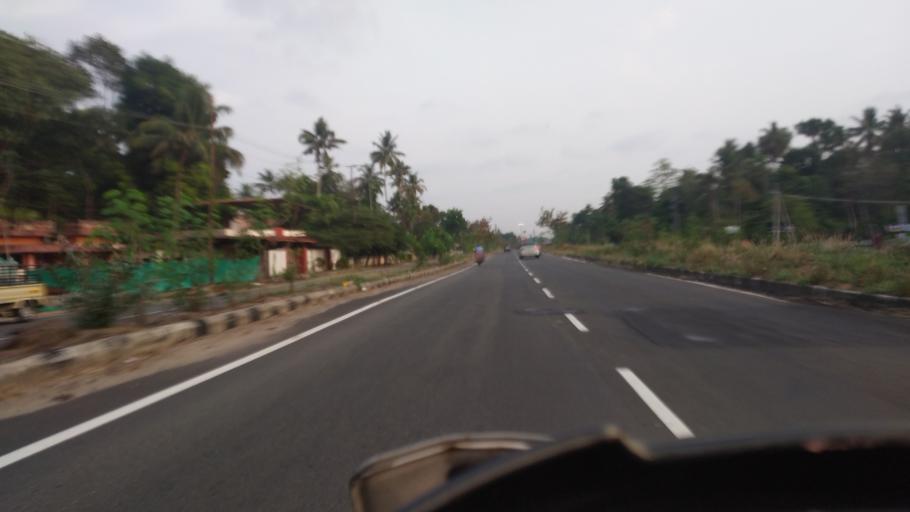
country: IN
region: Kerala
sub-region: Thrissur District
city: Kodungallur
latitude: 10.2156
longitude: 76.1973
